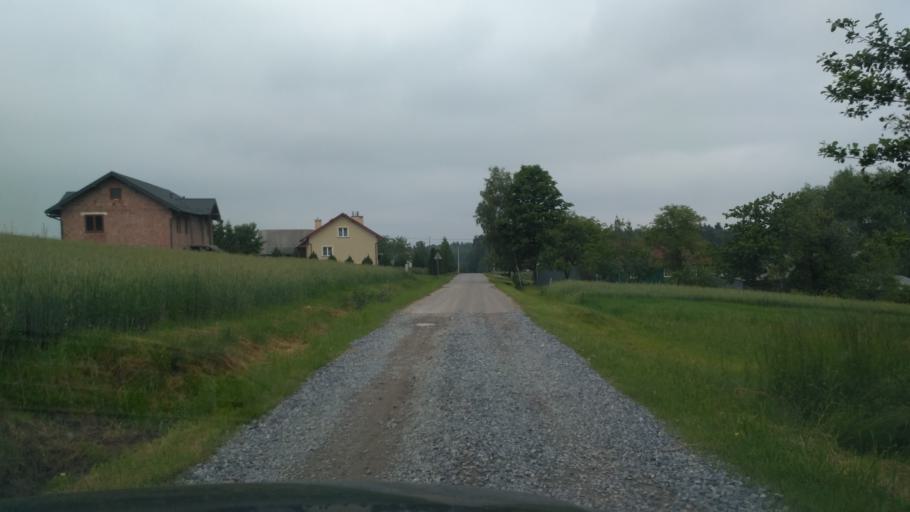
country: PL
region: Subcarpathian Voivodeship
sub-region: Powiat ropczycko-sedziszowski
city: Zagorzyce
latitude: 49.9879
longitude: 21.7059
